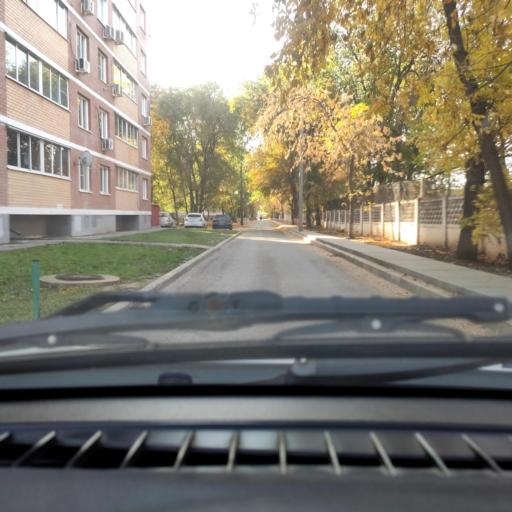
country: RU
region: Samara
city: Tol'yatti
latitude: 53.5036
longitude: 49.4178
